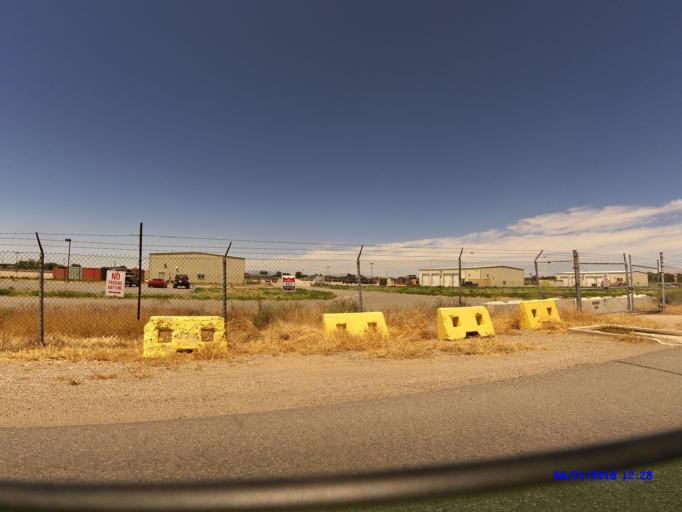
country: US
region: Utah
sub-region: Weber County
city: Harrisville
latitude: 41.2778
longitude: -111.9998
